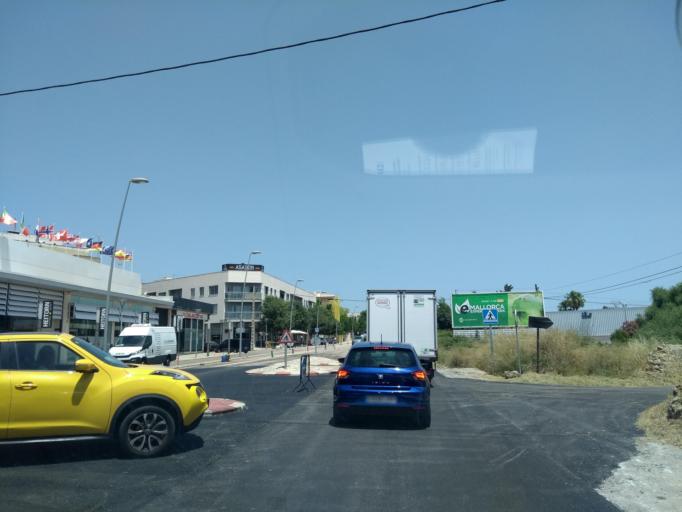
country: ES
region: Balearic Islands
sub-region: Illes Balears
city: Inca
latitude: 39.7239
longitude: 2.9199
